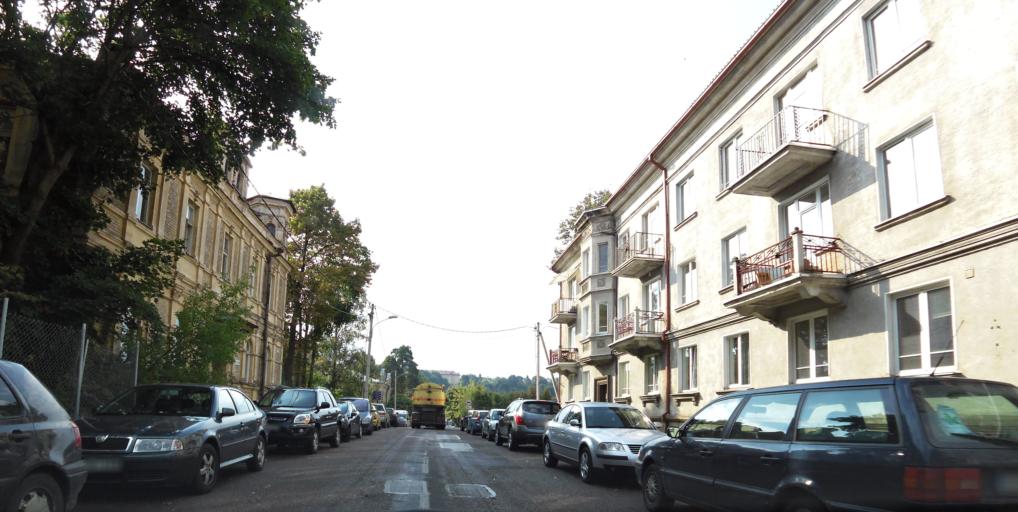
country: LT
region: Vilnius County
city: Naujamiestis
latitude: 54.6881
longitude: 25.2562
